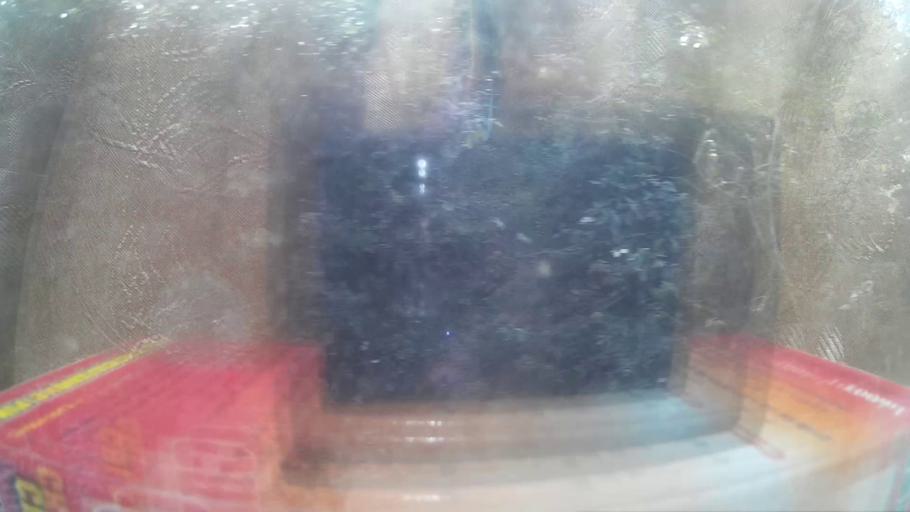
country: VN
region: Phu Yen
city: Chi Thanh
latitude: 13.3104
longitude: 109.1961
